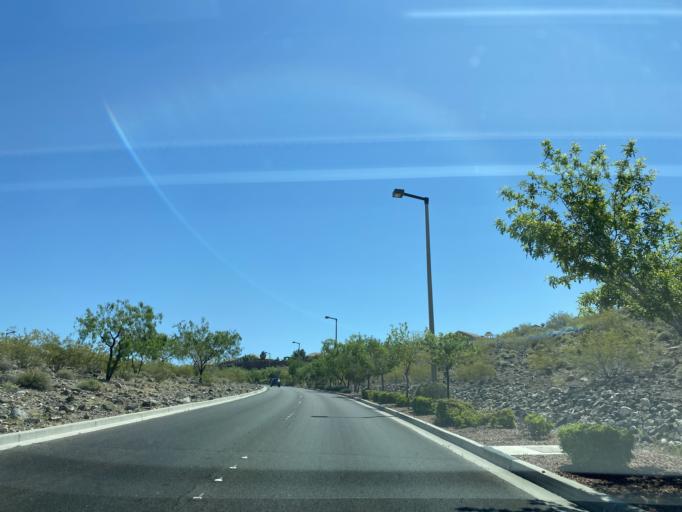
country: US
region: Nevada
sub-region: Clark County
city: Whitney
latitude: 35.9399
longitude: -115.1077
